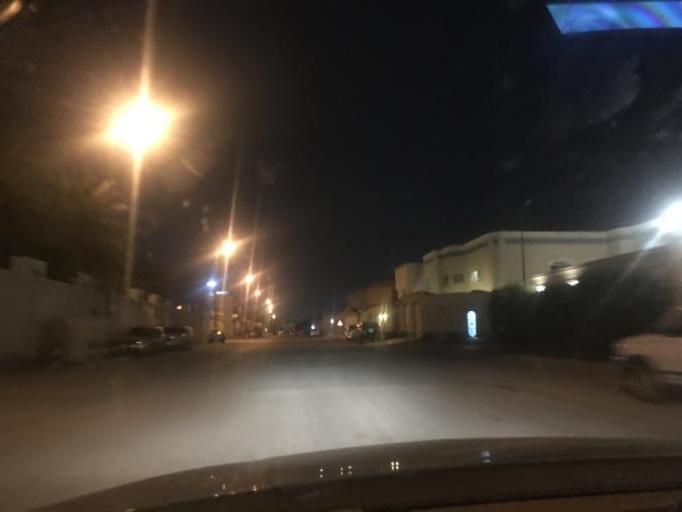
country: SA
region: Ar Riyad
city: Riyadh
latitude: 24.7435
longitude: 46.7853
